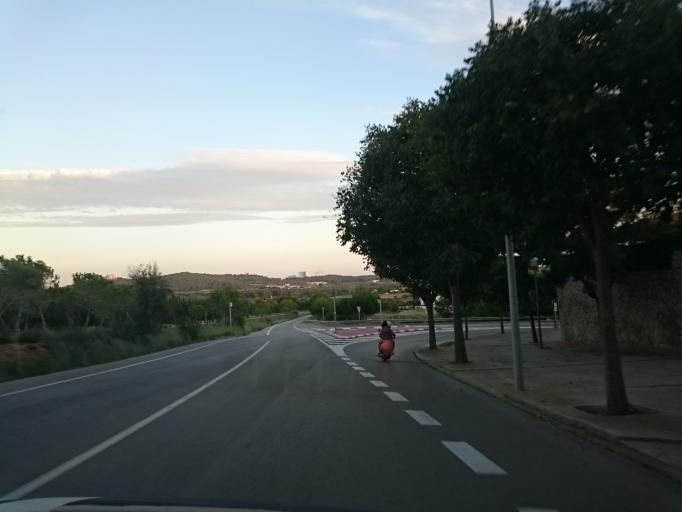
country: ES
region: Catalonia
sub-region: Provincia de Barcelona
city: Sant Pere de Ribes
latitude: 41.2630
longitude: 1.7815
